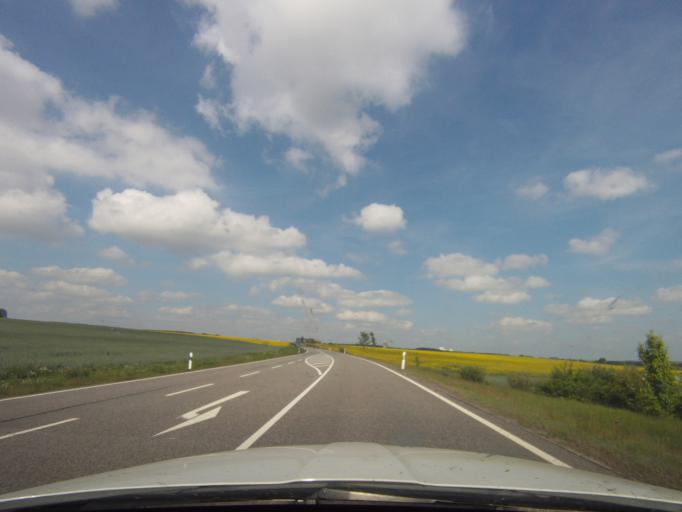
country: DE
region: Thuringia
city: Mittelpollnitz
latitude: 50.7595
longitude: 11.9186
